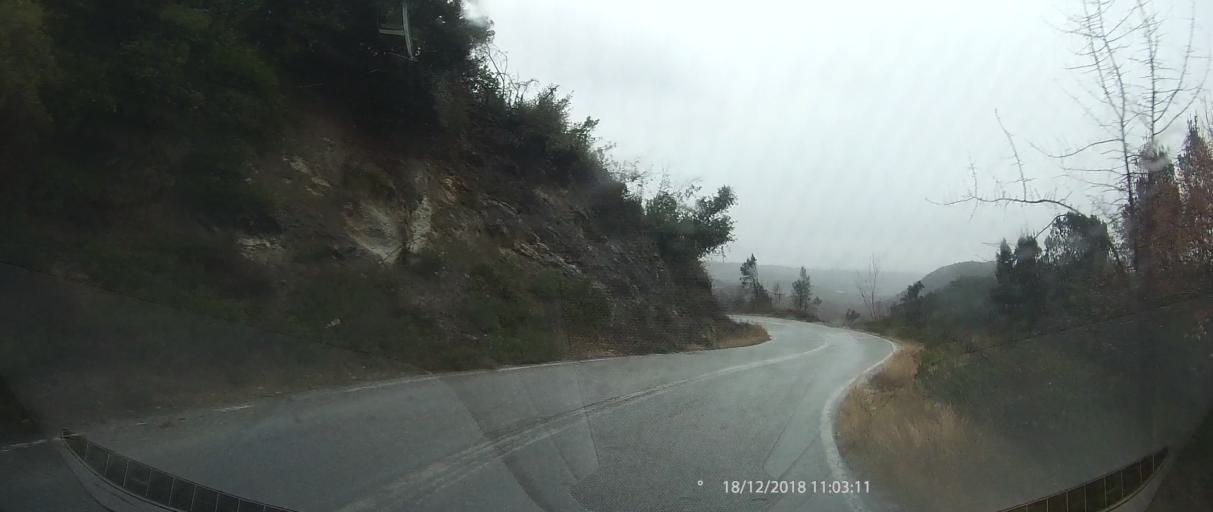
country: GR
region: Central Macedonia
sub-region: Nomos Pierias
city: Kato Milia
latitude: 40.2067
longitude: 22.3172
